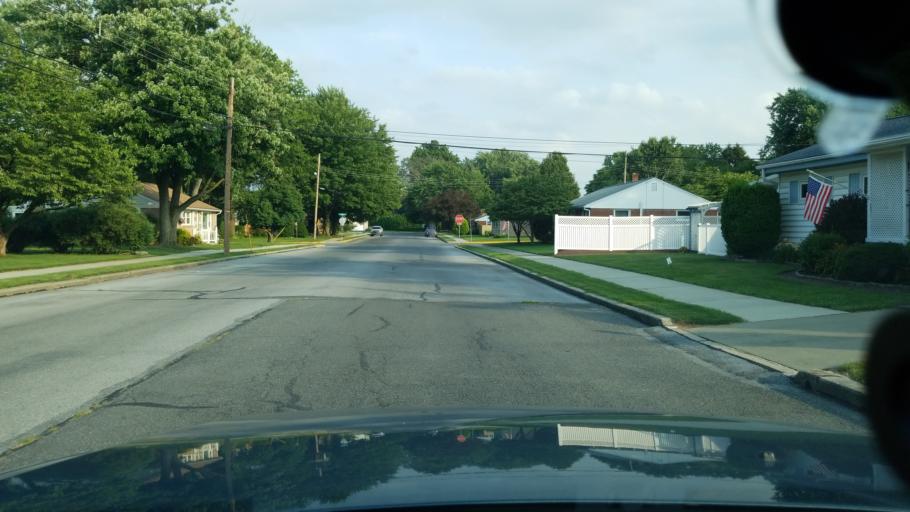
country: US
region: Pennsylvania
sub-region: Lebanon County
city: Palmyra
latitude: 40.3083
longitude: -76.5802
